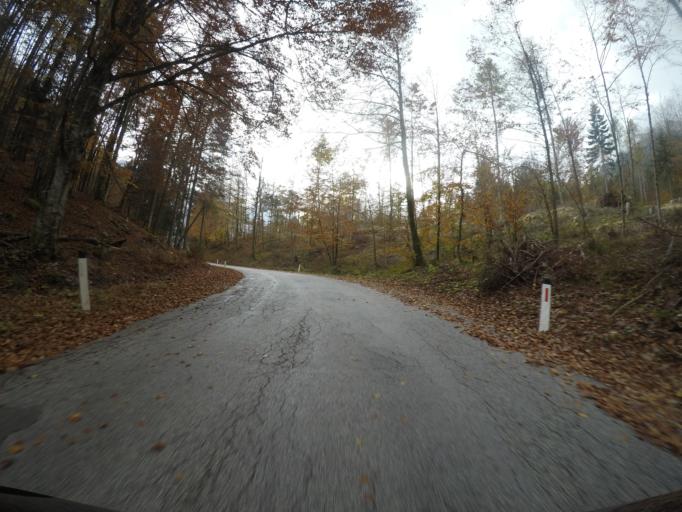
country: SI
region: Kranjska Gora
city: Mojstrana
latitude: 46.4392
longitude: 13.9311
